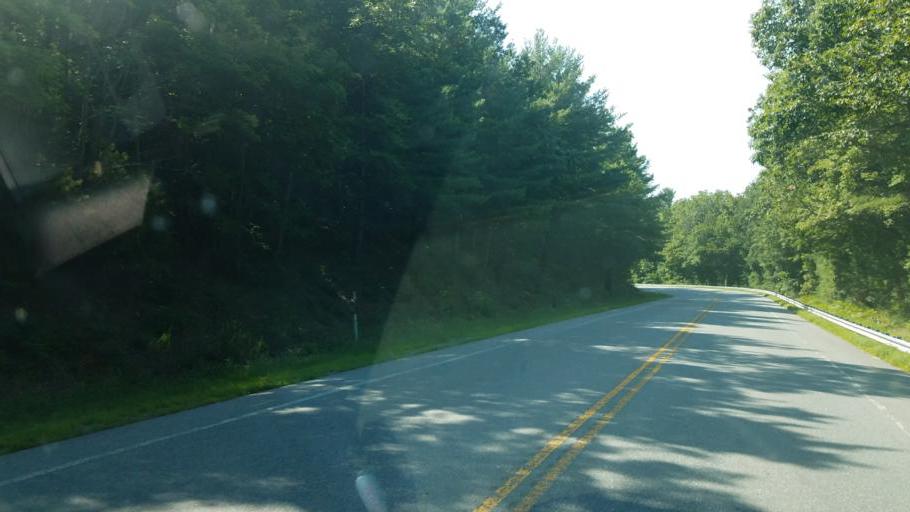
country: US
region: North Carolina
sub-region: Avery County
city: Newland
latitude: 35.9562
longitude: -81.8582
